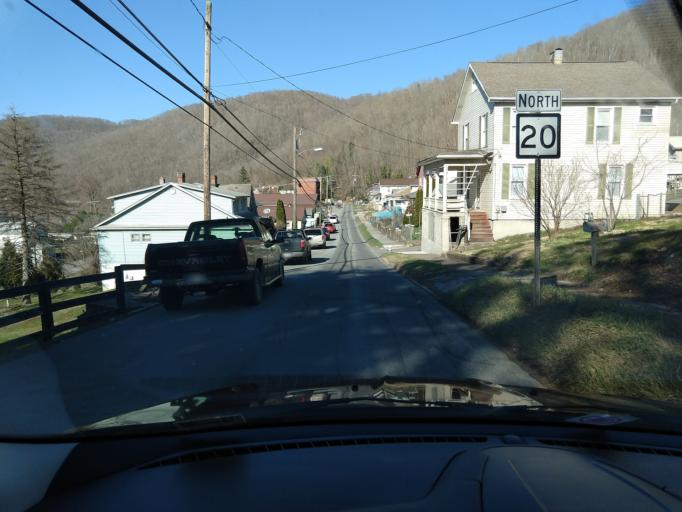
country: US
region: West Virginia
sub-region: Summers County
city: Hinton
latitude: 37.6820
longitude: -80.8759
